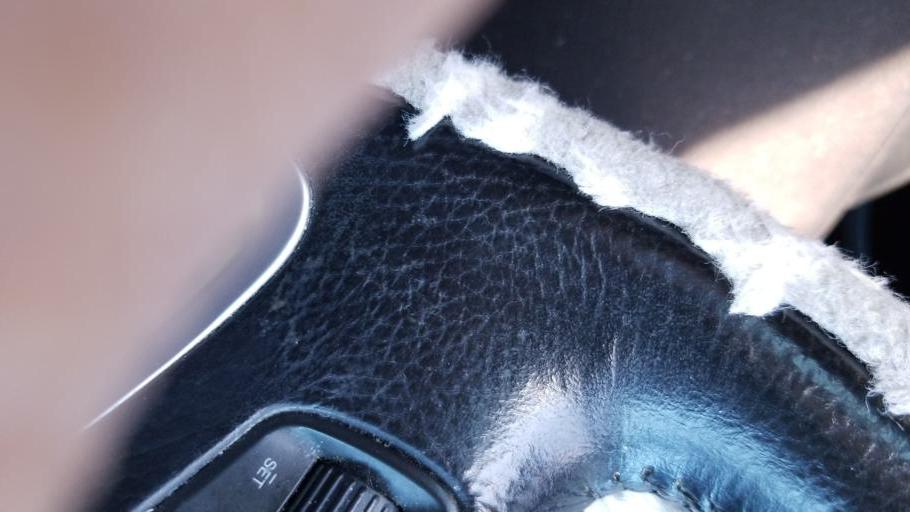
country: US
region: Texas
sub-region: Dallas County
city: Cockrell Hill
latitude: 32.7308
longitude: -96.8448
